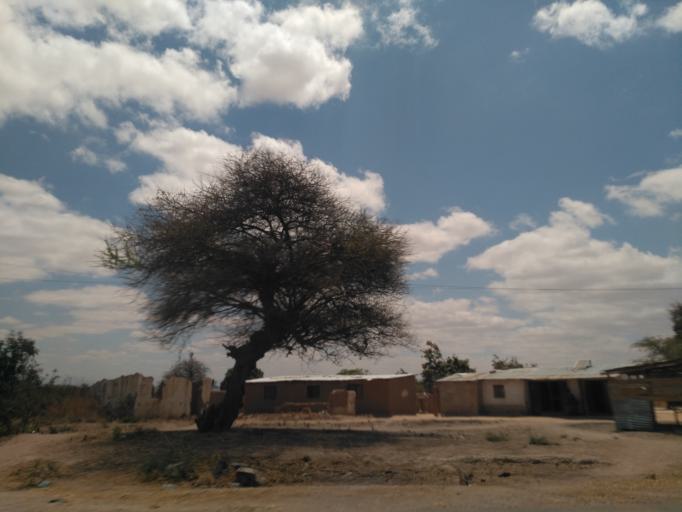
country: TZ
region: Dodoma
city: Kisasa
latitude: -6.1715
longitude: 35.7944
